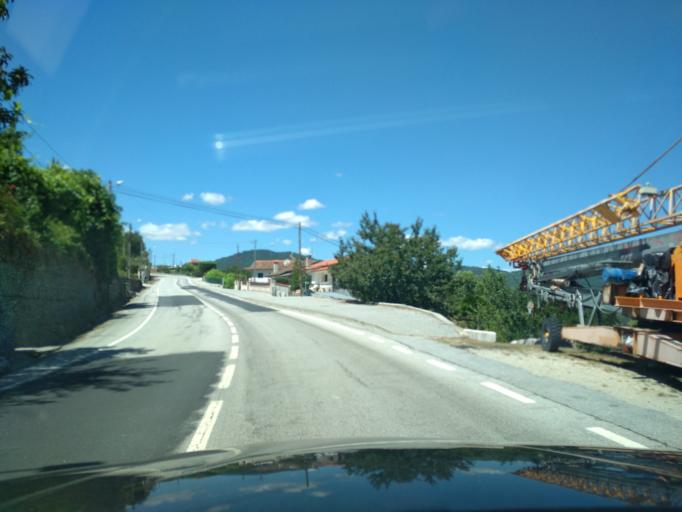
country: PT
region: Vila Real
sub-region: Ribeira de Pena
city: Sobreira
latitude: 41.5237
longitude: -7.7876
